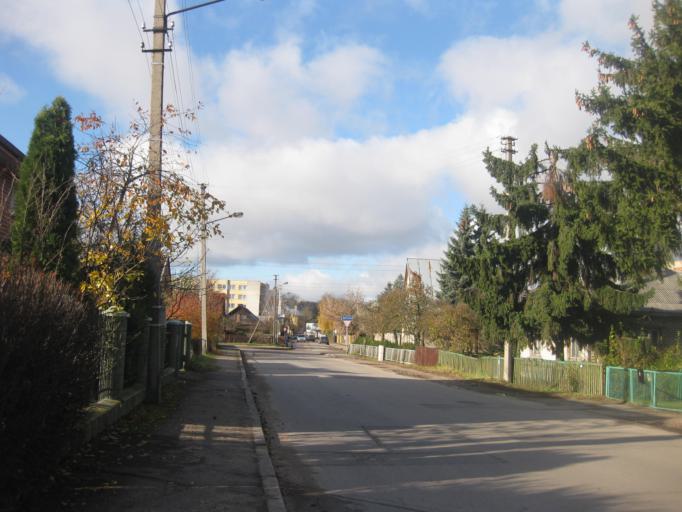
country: LT
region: Kauno apskritis
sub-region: Kaunas
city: Kaunas
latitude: 54.9094
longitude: 23.8884
